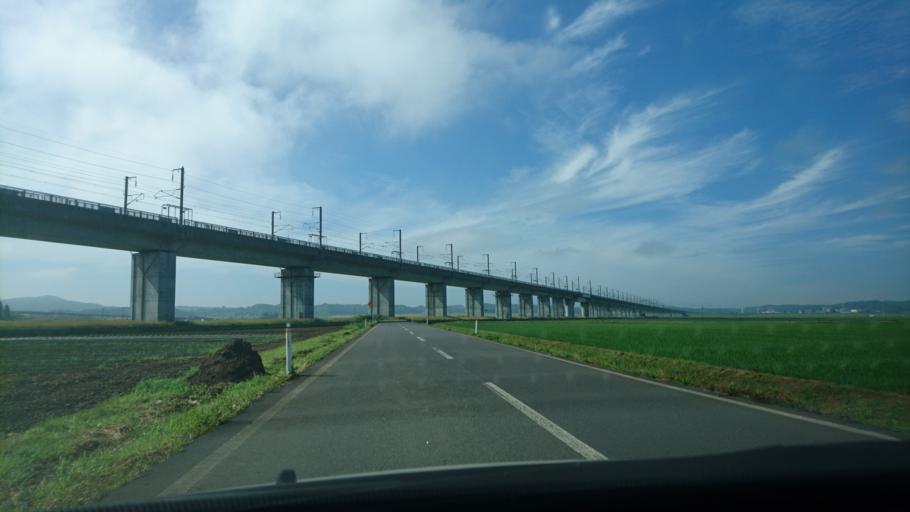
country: JP
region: Iwate
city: Ichinoseki
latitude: 38.9598
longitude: 141.1505
